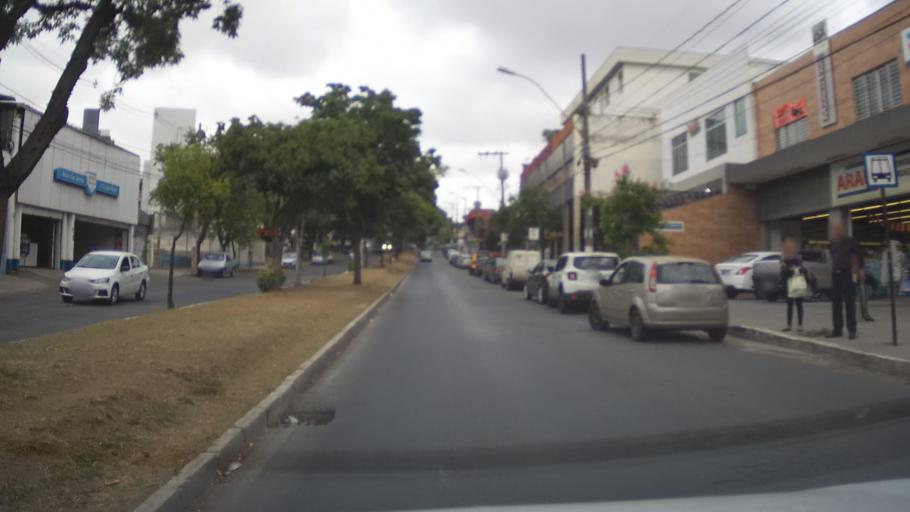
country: BR
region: Minas Gerais
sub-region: Belo Horizonte
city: Belo Horizonte
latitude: -19.8612
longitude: -43.9444
